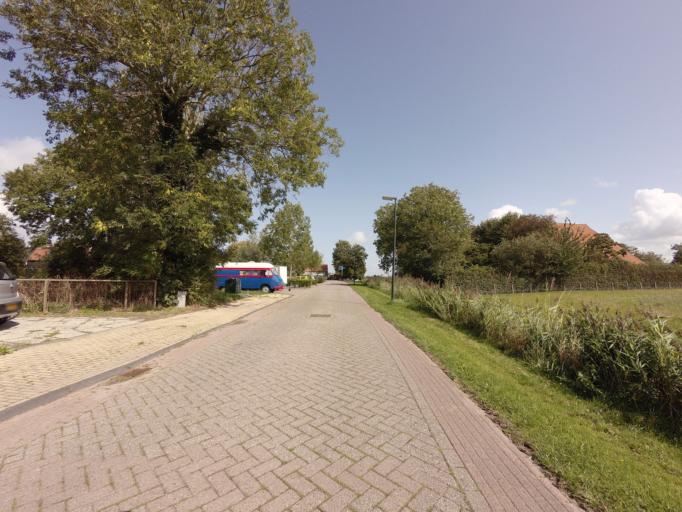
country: NL
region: Friesland
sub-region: Sudwest Fryslan
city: Makkum
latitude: 53.0801
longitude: 5.4524
